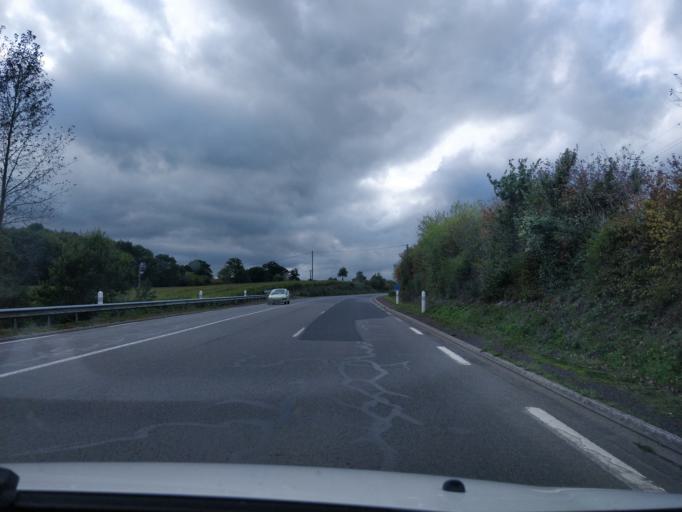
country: FR
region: Lower Normandy
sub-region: Departement du Calvados
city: Saint-Sever-Calvados
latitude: 48.8389
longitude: -1.0154
